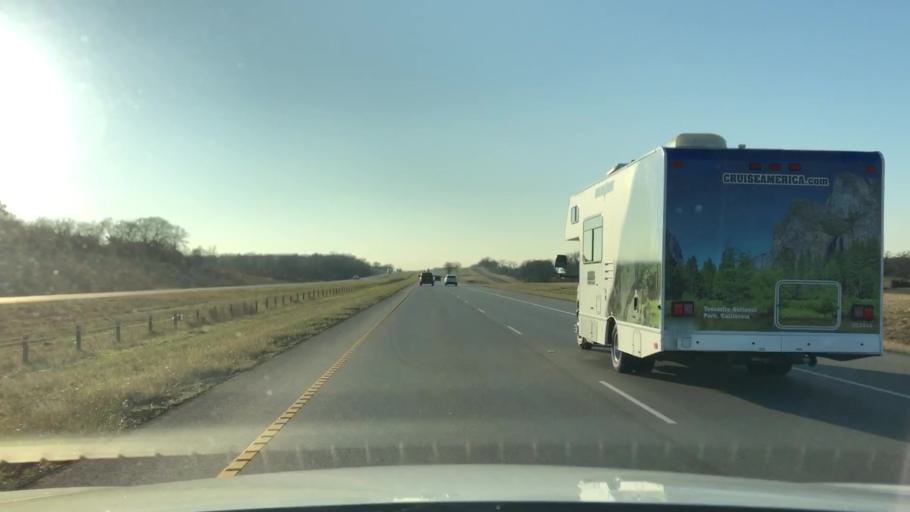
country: US
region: Texas
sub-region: Gonzales County
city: Waelder
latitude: 29.6566
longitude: -97.4374
